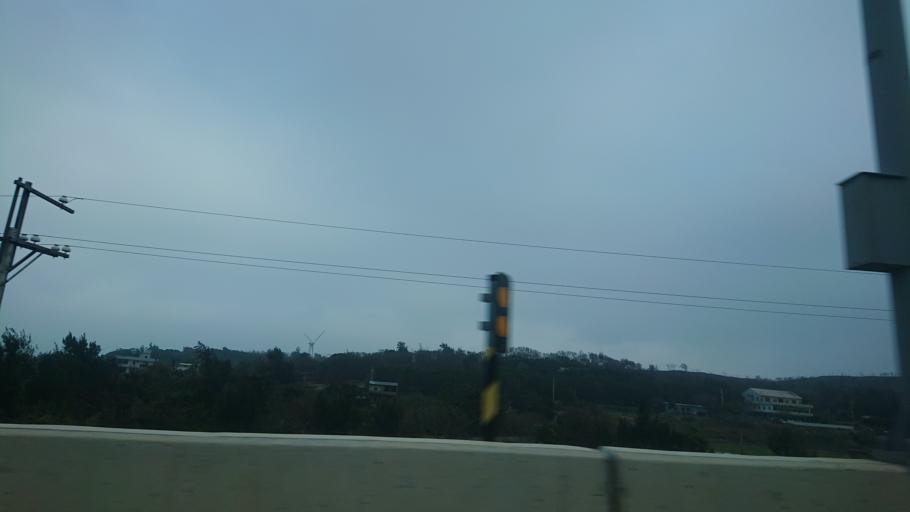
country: TW
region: Taiwan
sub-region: Miaoli
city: Miaoli
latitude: 24.5716
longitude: 120.7170
